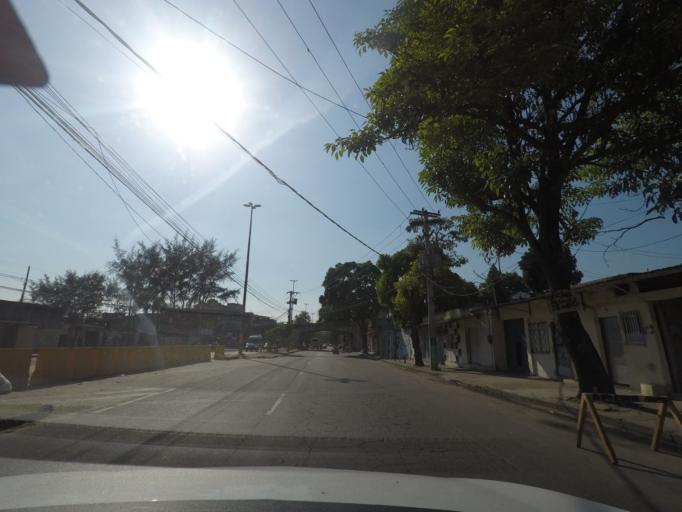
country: BR
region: Rio de Janeiro
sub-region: Rio De Janeiro
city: Rio de Janeiro
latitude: -22.8880
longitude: -43.2462
